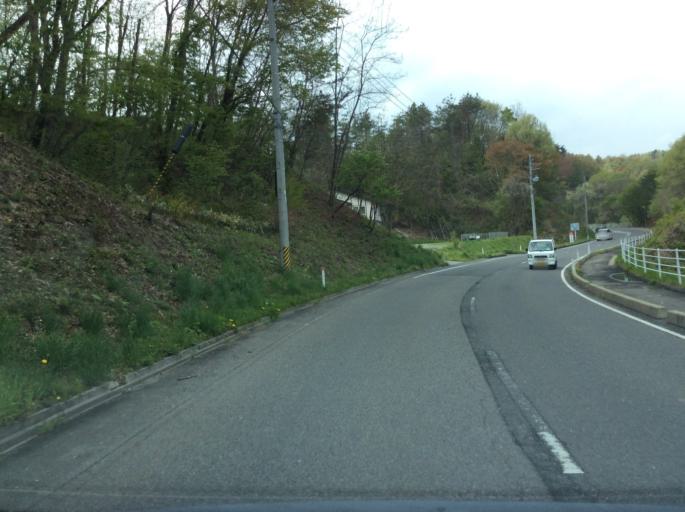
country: JP
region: Fukushima
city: Miharu
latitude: 37.3959
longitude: 140.4822
